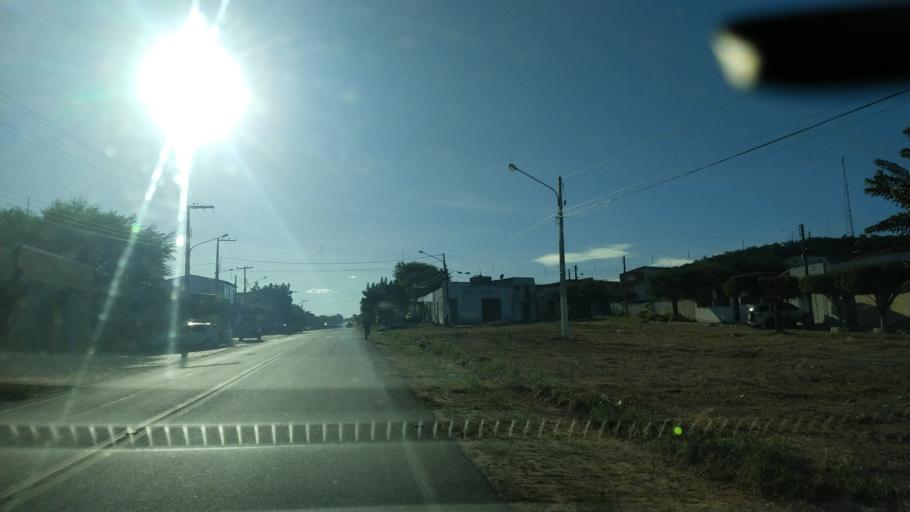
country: BR
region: Rio Grande do Norte
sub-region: Sao Jose Do Campestre
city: Sao Jose do Campestre
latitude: -6.3185
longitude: -35.7078
